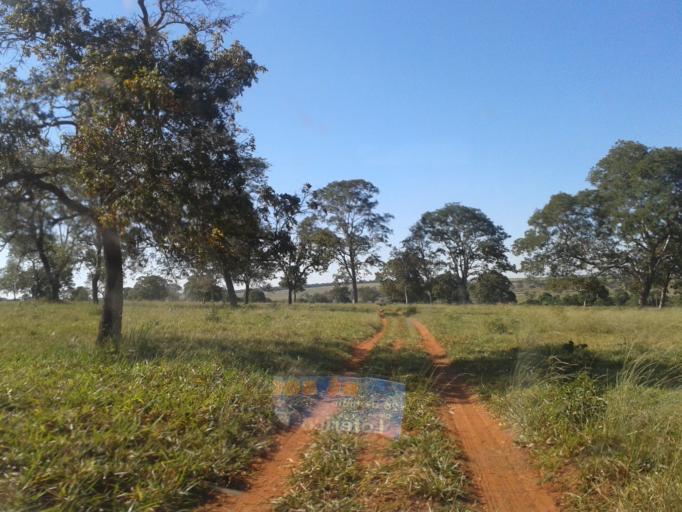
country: BR
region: Minas Gerais
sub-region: Santa Vitoria
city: Santa Vitoria
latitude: -19.0403
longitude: -50.3810
